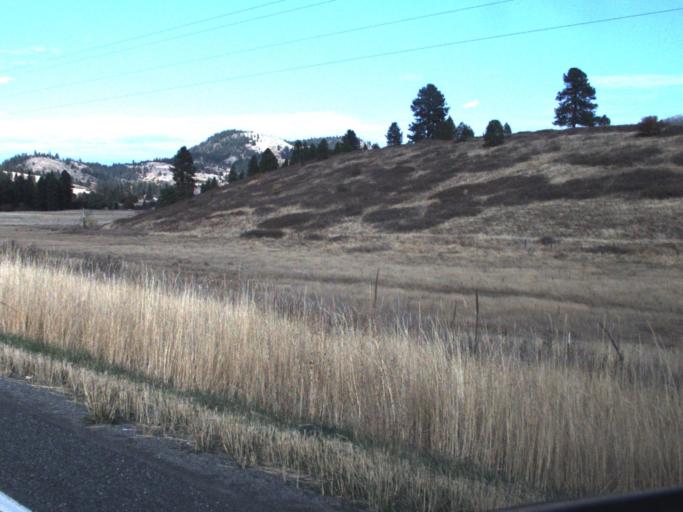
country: US
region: Washington
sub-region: Stevens County
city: Kettle Falls
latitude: 48.4444
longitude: -118.1707
